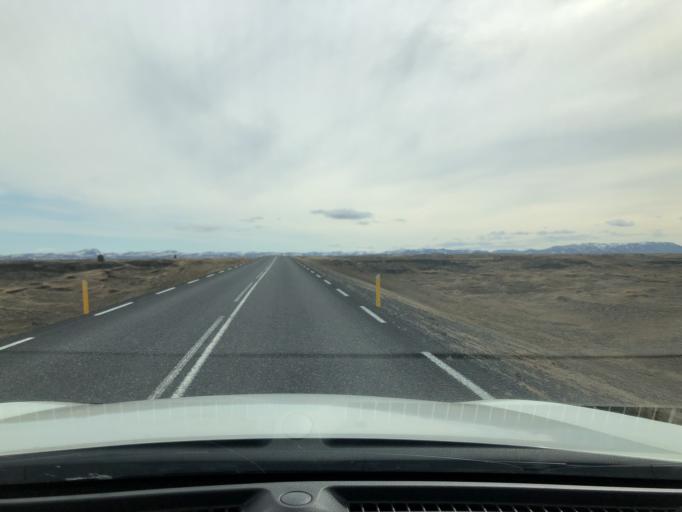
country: IS
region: Northeast
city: Laugar
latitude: 65.6466
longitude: -16.3598
